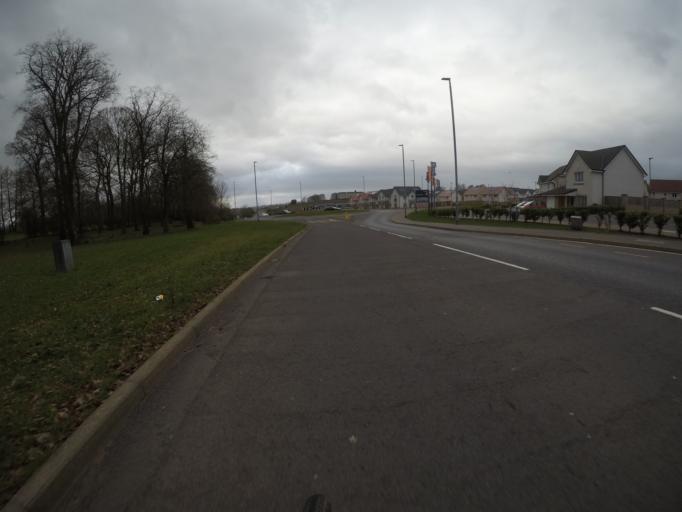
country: GB
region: Scotland
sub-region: East Ayrshire
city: Crosshouse
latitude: 55.6116
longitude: -4.5245
